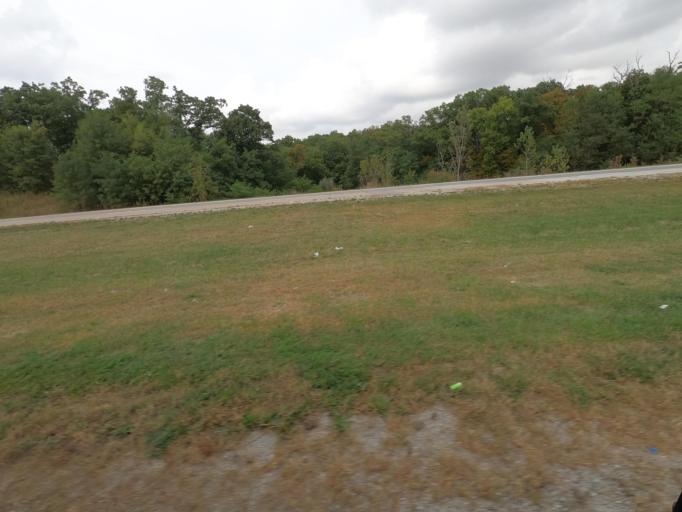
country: US
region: Iowa
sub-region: Wapello County
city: Ottumwa
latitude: 40.9984
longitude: -92.3354
